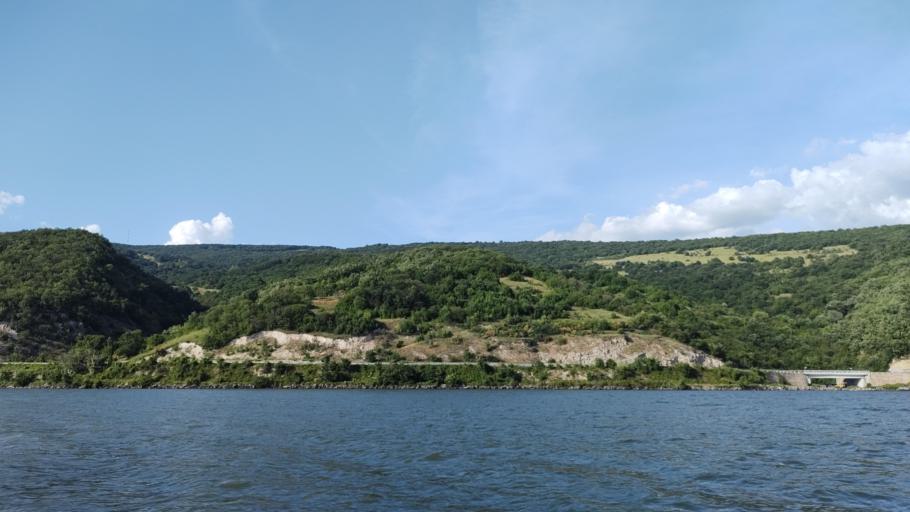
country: RO
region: Mehedinti
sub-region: Comuna Svinita
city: Svinita
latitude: 44.4870
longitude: 22.1129
